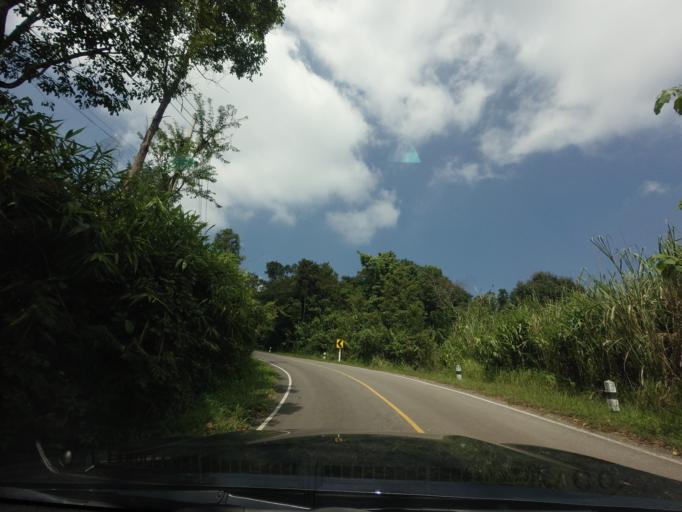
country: TH
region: Loei
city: Na Haeo
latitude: 17.4816
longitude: 100.9148
